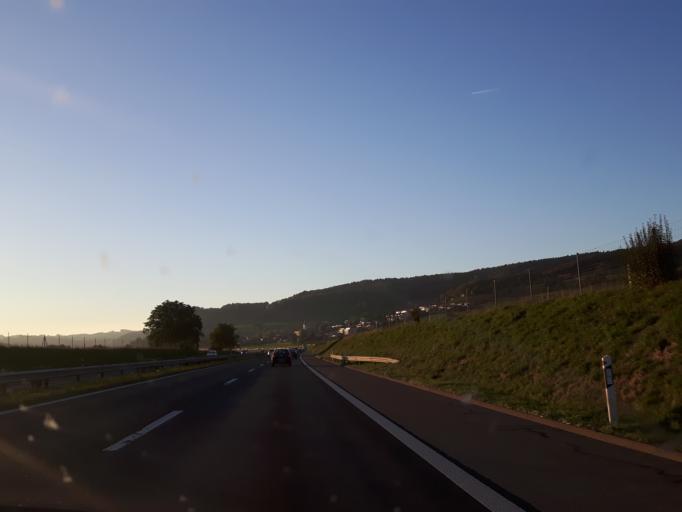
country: CH
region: Lucerne
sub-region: Willisau District
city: Wauwil
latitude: 47.2050
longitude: 8.0388
